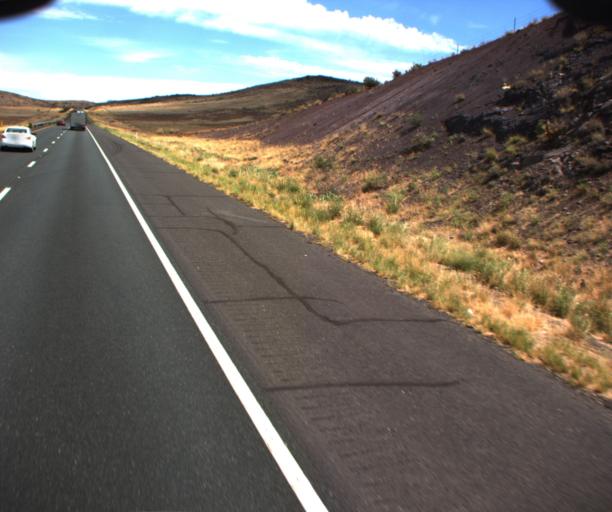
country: US
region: Arizona
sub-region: Yavapai County
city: Cordes Lakes
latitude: 34.4462
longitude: -112.0308
